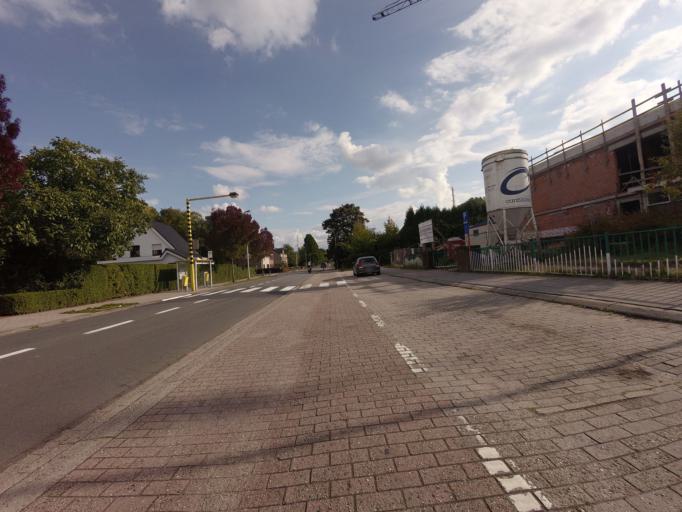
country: BE
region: Flanders
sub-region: Provincie Antwerpen
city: Boom
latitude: 51.1049
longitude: 4.3867
